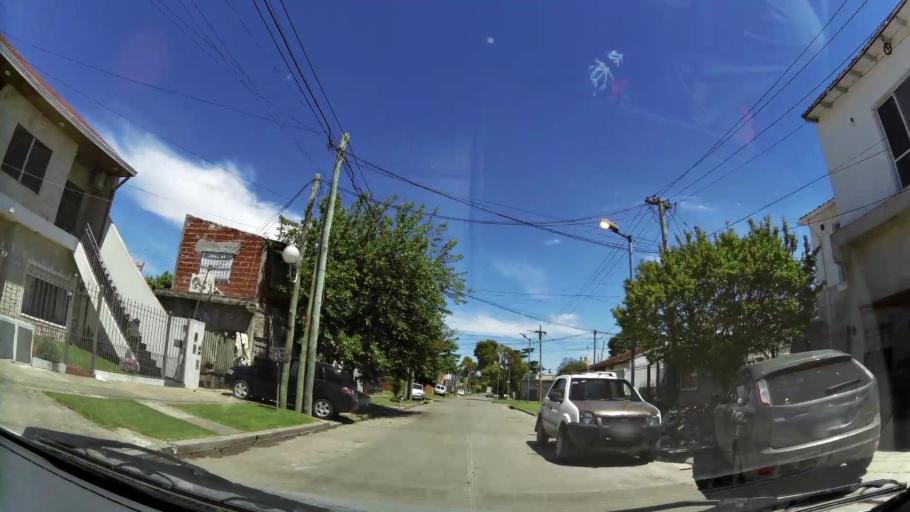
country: AR
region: Buenos Aires
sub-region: Partido de Quilmes
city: Quilmes
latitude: -34.7460
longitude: -58.2820
